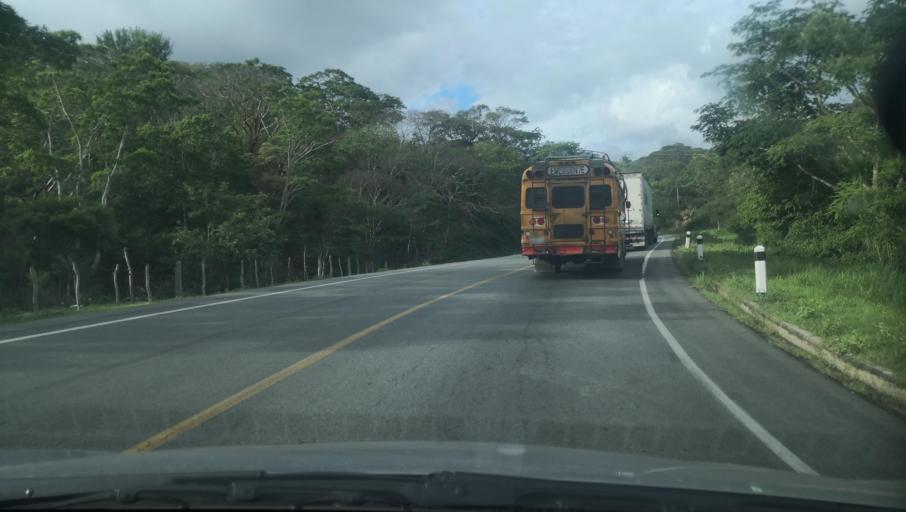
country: NI
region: Nueva Segovia
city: Ocotal
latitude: 13.6868
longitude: -86.4884
